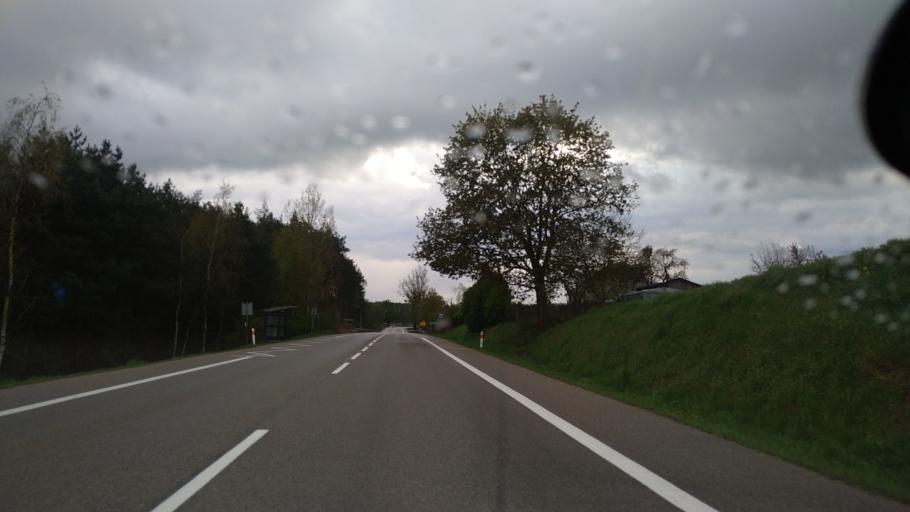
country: PL
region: Pomeranian Voivodeship
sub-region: Powiat starogardzki
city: Smetowo Graniczne
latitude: 53.7394
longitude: 18.7420
